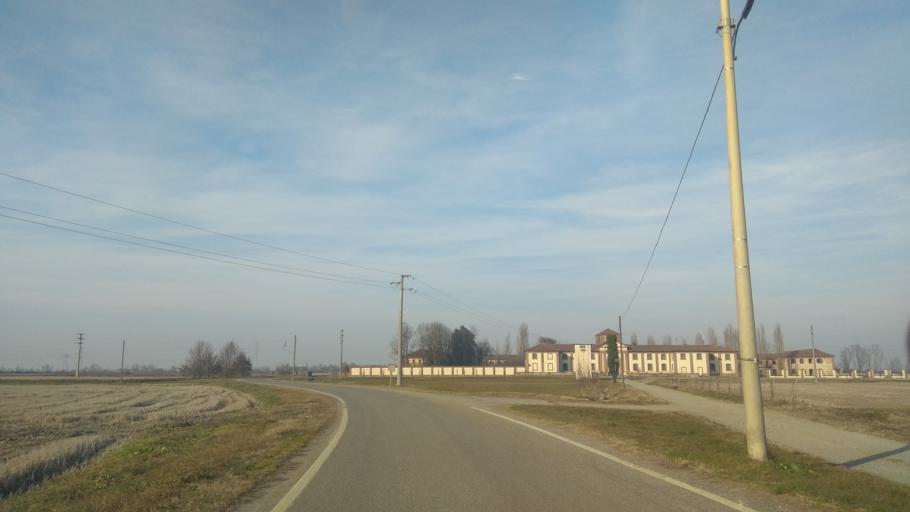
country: IT
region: Piedmont
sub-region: Provincia di Vercelli
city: Ronsecco
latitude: 45.2472
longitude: 8.2359
